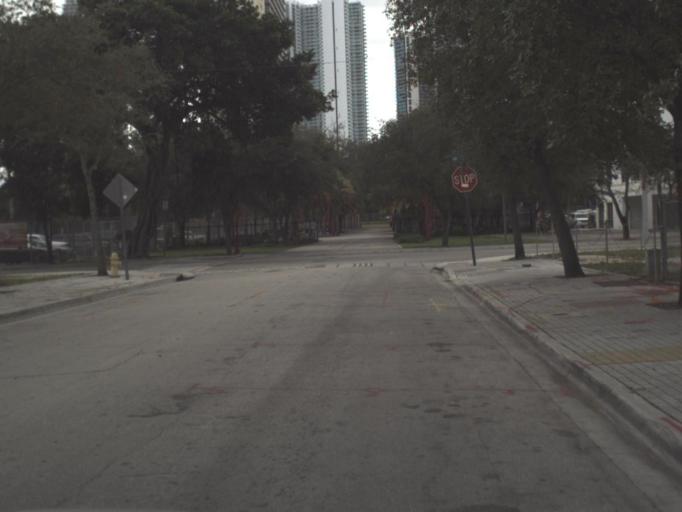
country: US
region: Florida
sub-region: Miami-Dade County
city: Miami
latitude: 25.7827
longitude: -80.1984
